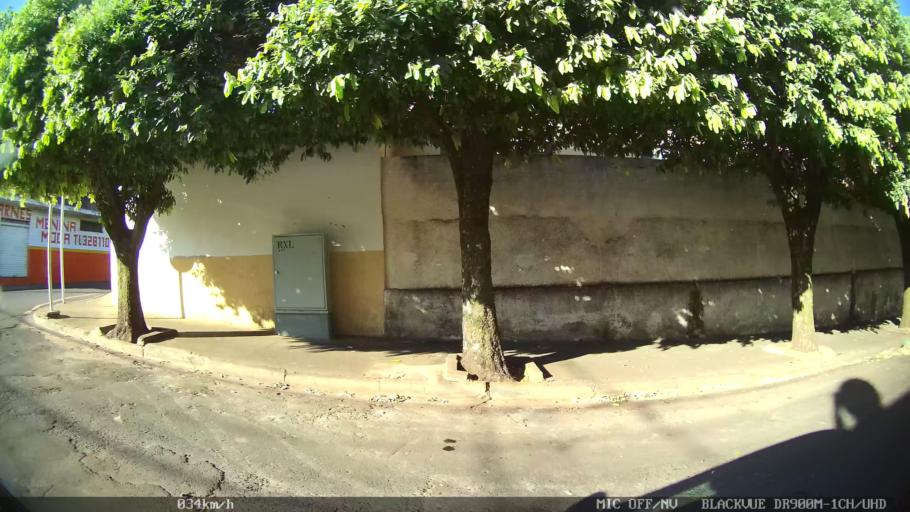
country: BR
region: Sao Paulo
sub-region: Olimpia
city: Olimpia
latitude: -20.7336
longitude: -48.9080
